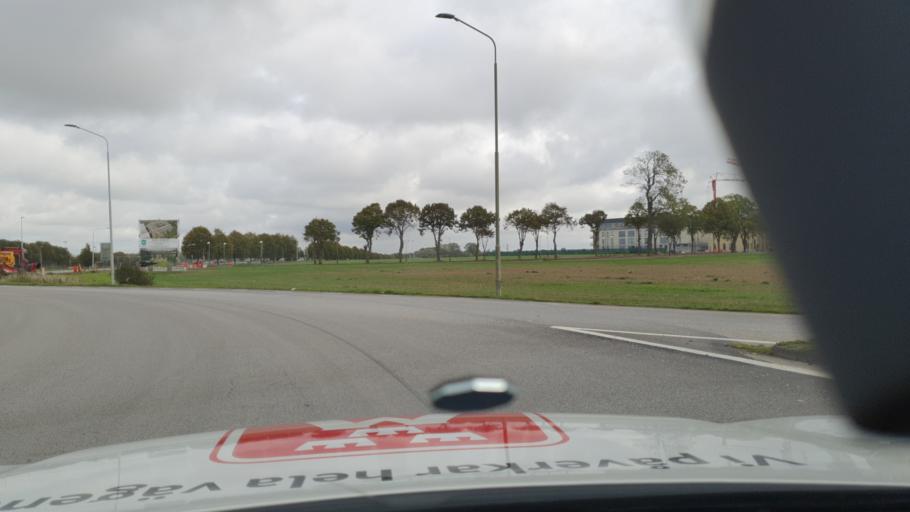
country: SE
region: Skane
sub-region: Burlovs Kommun
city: Arloev
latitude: 55.6398
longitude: 13.0892
